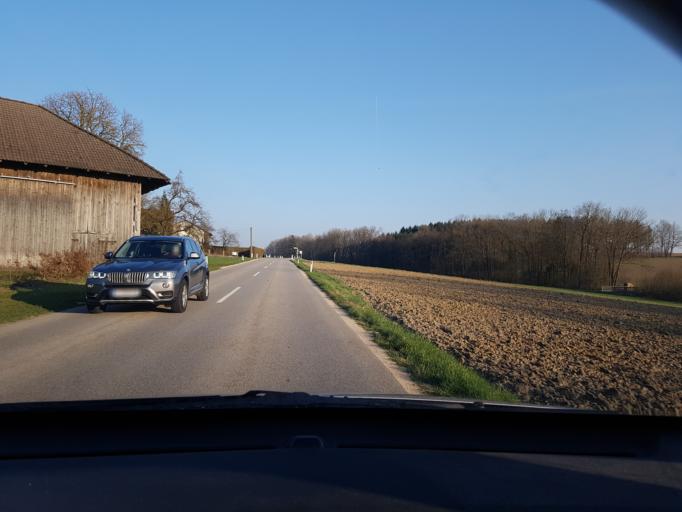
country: AT
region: Upper Austria
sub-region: Politischer Bezirk Linz-Land
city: Ansfelden
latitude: 48.1561
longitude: 14.2564
